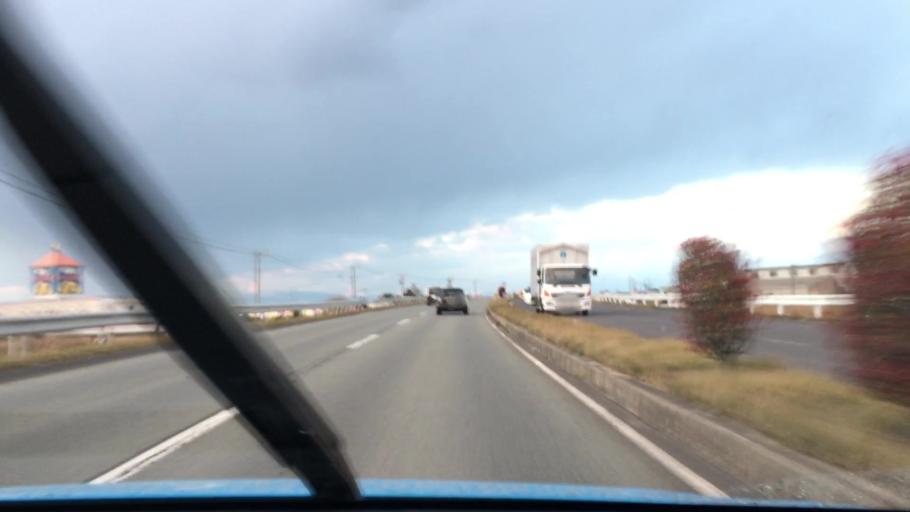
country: JP
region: Mie
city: Ise
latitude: 34.5442
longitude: 136.6612
